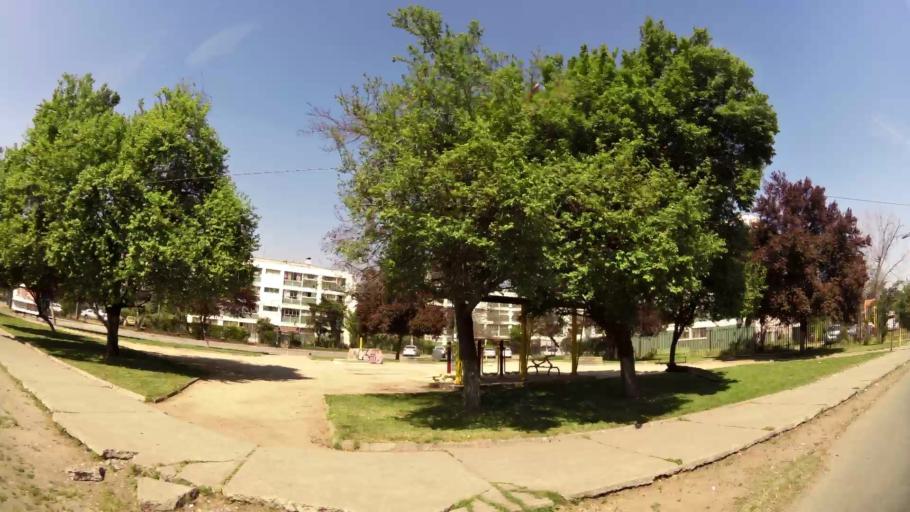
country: CL
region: Santiago Metropolitan
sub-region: Provincia de Santiago
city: Villa Presidente Frei, Nunoa, Santiago, Chile
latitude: -33.4739
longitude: -70.5868
